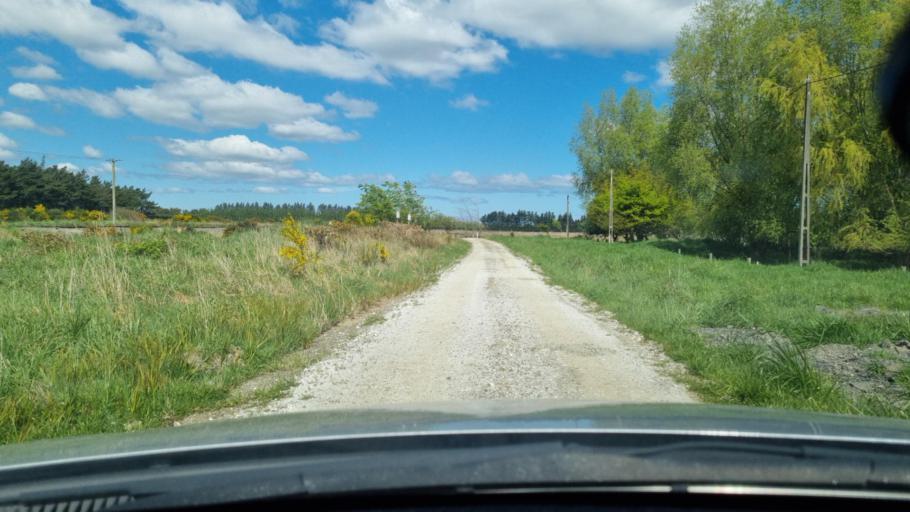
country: NZ
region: Southland
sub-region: Invercargill City
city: Invercargill
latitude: -46.3487
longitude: 168.3400
